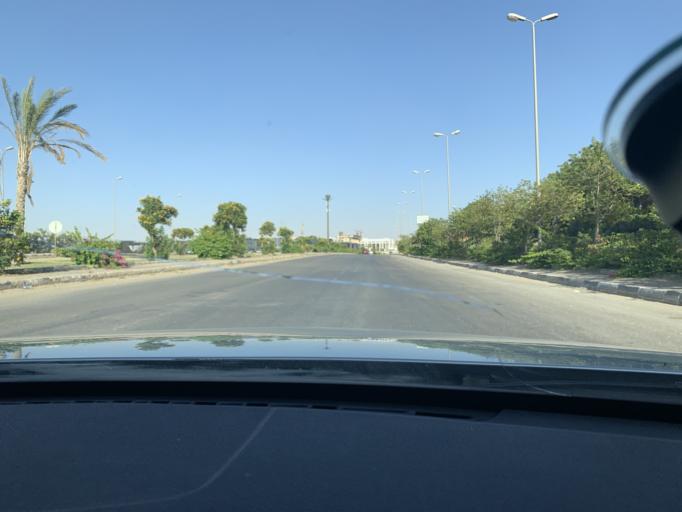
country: EG
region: Muhafazat al Qalyubiyah
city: Al Khankah
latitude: 30.0519
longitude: 31.5081
